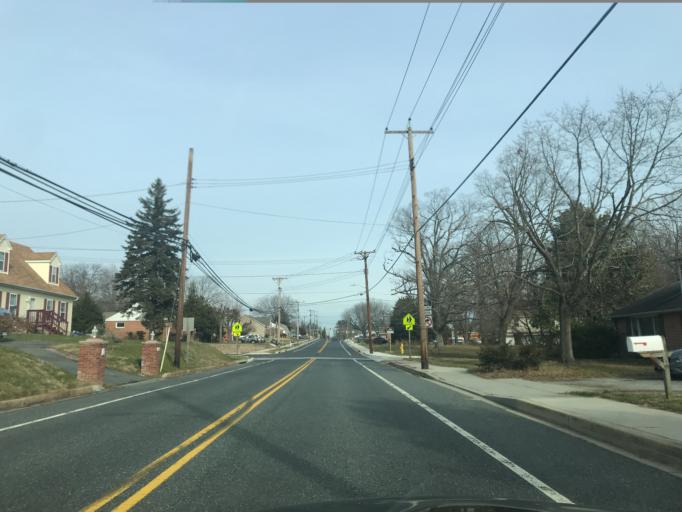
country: US
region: Maryland
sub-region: Harford County
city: Aberdeen
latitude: 39.5188
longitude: -76.1712
